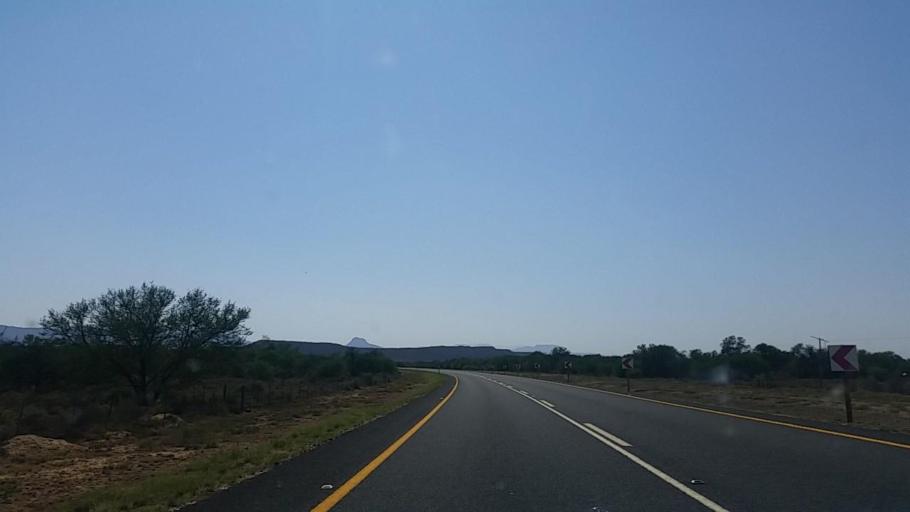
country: ZA
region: Eastern Cape
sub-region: Cacadu District Municipality
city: Graaff-Reinet
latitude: -32.3463
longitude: 24.3619
